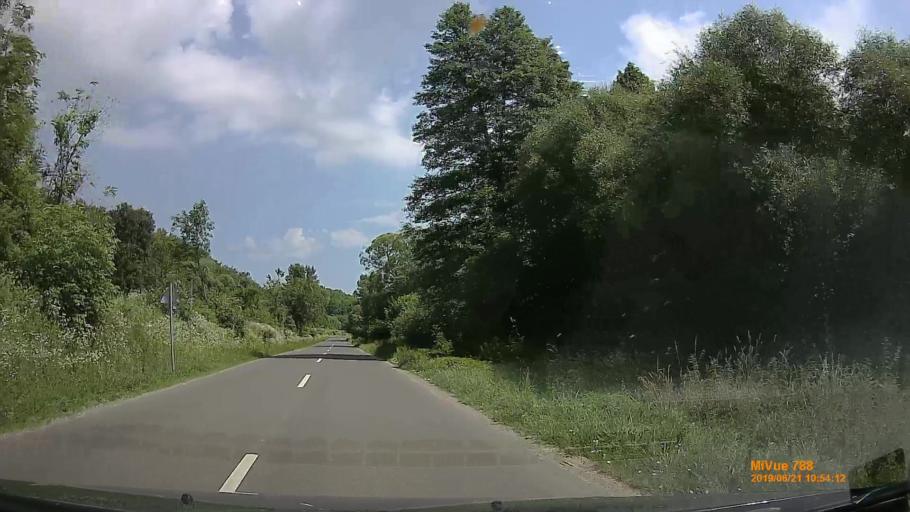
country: HU
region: Baranya
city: Buekkoesd
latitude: 46.1509
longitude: 18.0640
